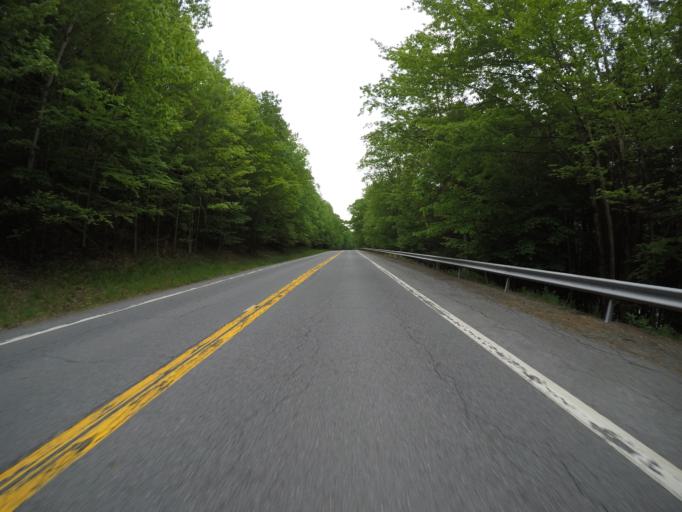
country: US
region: New York
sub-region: Sullivan County
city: Livingston Manor
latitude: 42.0763
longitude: -74.8847
